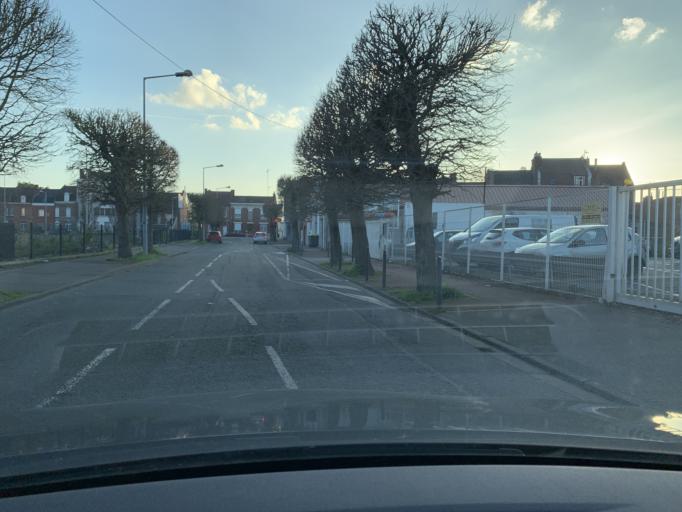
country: FR
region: Nord-Pas-de-Calais
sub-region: Departement du Nord
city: Douai
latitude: 50.3591
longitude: 3.0816
